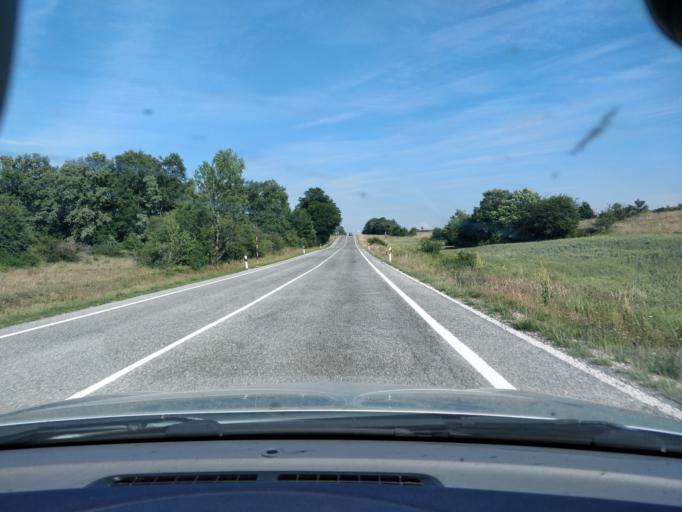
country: ES
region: Cantabria
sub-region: Provincia de Cantabria
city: San Martin de Elines
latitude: 42.9393
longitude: -3.7331
